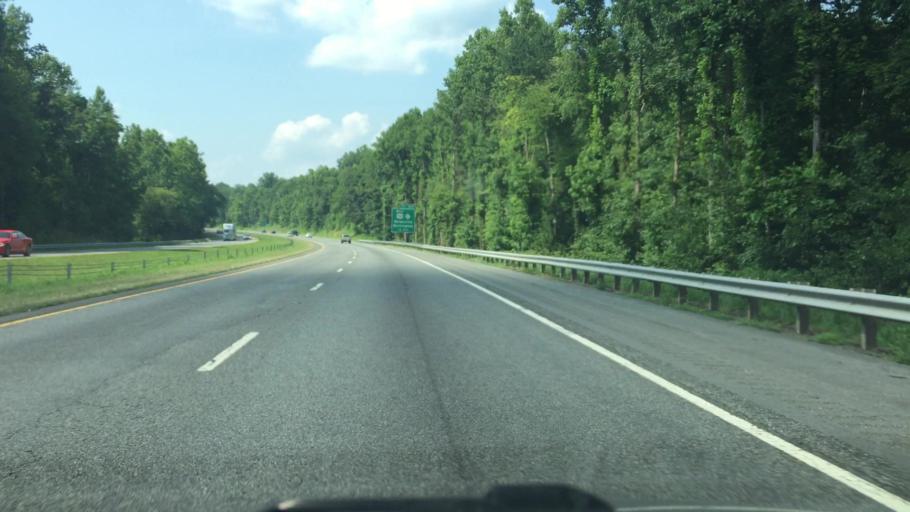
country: US
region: North Carolina
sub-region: Rockingham County
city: Reidsville
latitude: 36.2971
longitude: -79.6412
